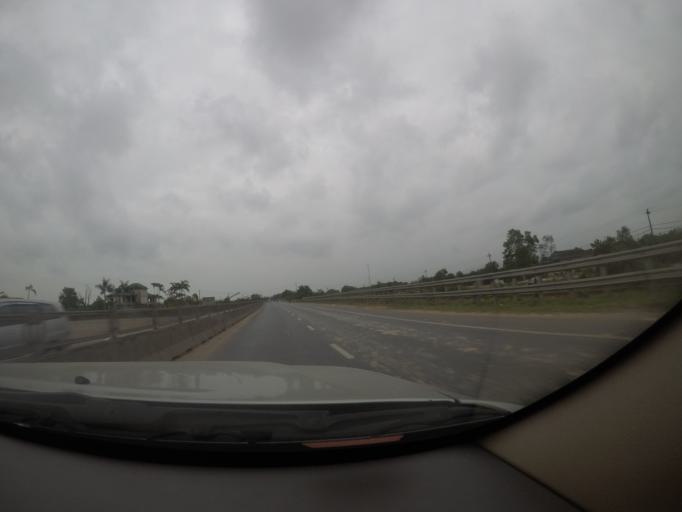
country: VN
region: Quang Tri
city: Hai Lang
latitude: 16.7087
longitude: 107.2191
